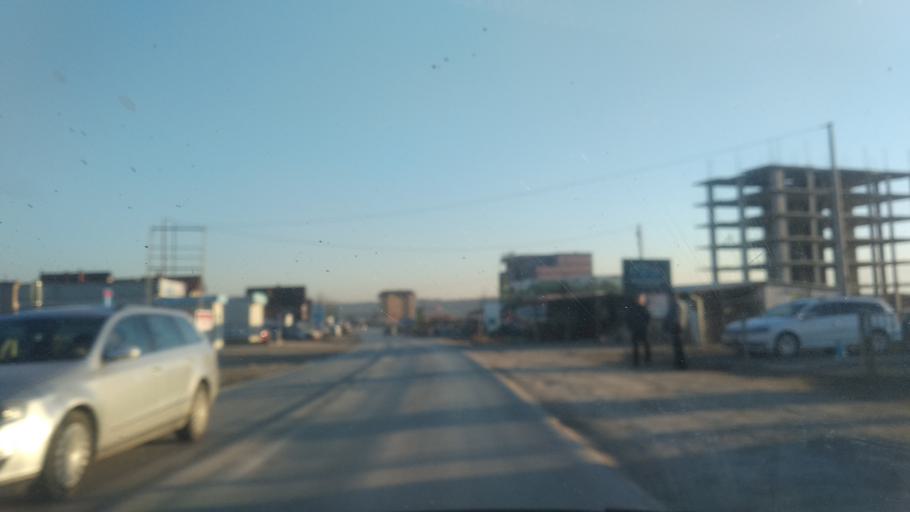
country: XK
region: Pristina
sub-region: Komuna e Prishtines
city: Pristina
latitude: 42.6149
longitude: 21.1713
